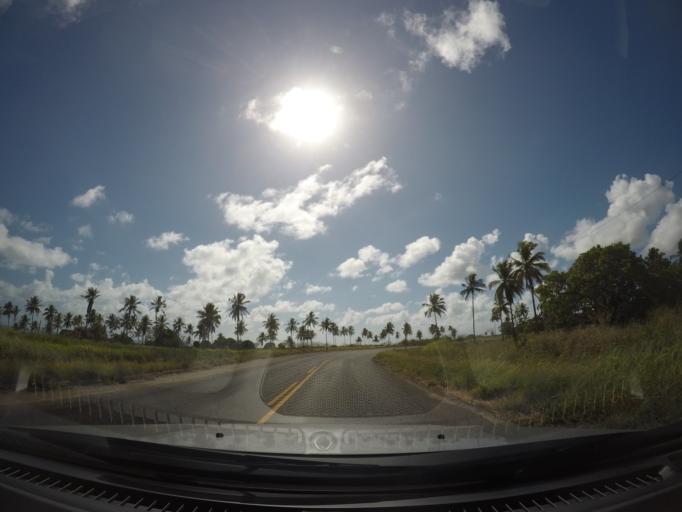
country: BR
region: Paraiba
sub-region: Pitimbu
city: Pitimbu
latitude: -7.3878
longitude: -34.8240
